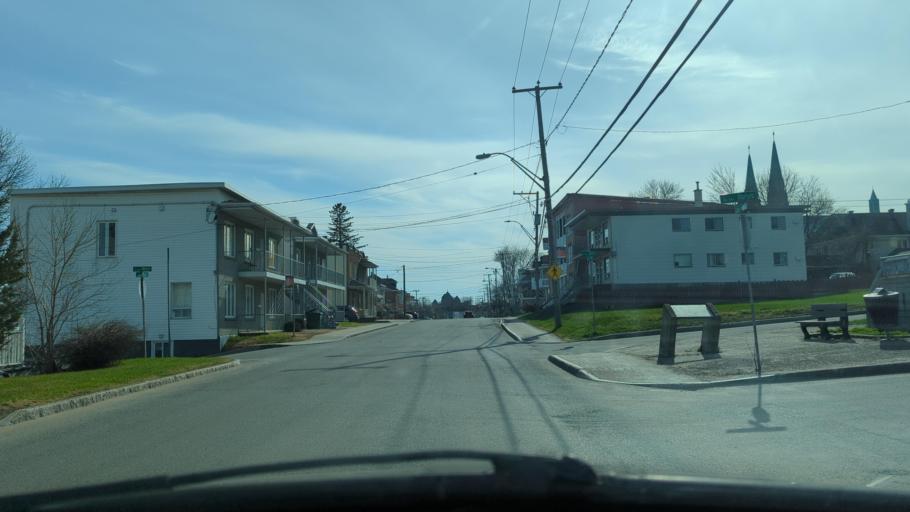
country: CA
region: Quebec
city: Quebec
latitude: 46.8533
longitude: -71.2056
